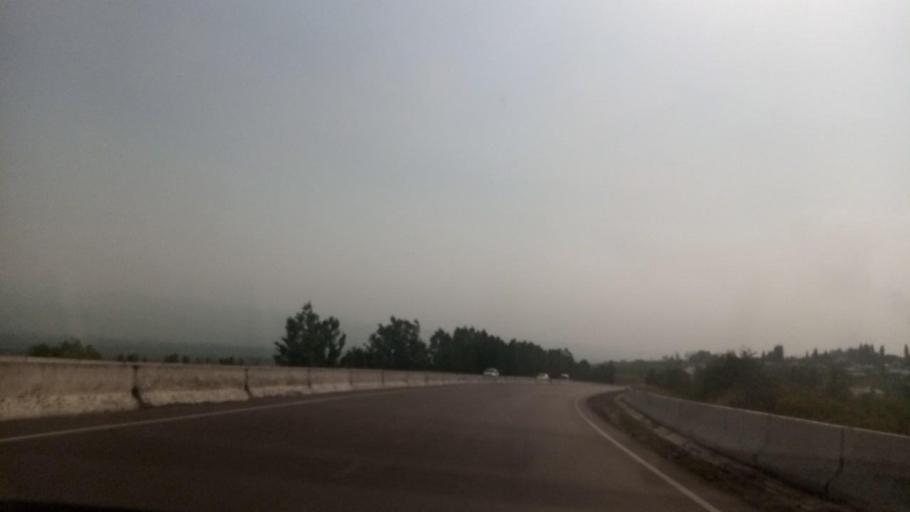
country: UZ
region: Toshkent
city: Angren
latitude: 40.9421
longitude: 69.9057
